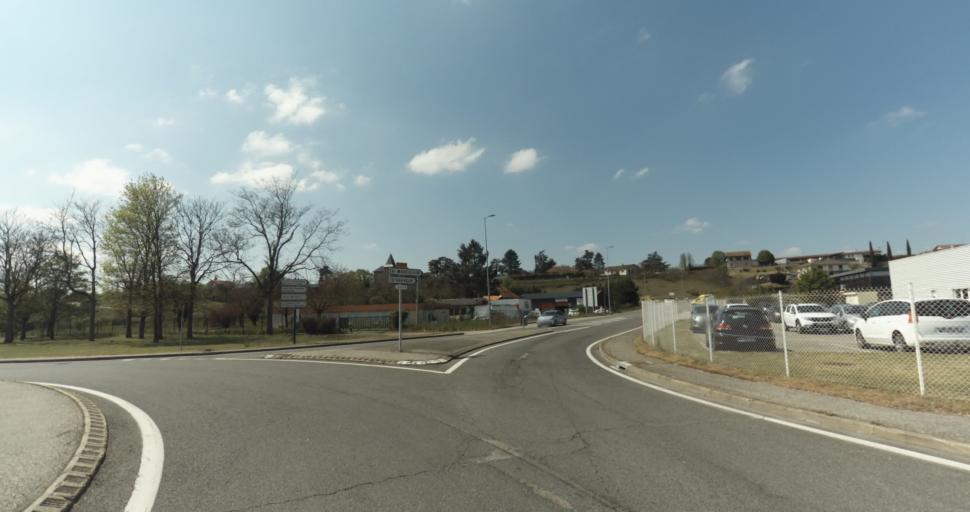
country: FR
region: Rhone-Alpes
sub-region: Departement de l'Isere
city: Saint-Marcellin
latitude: 45.1397
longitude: 5.3273
